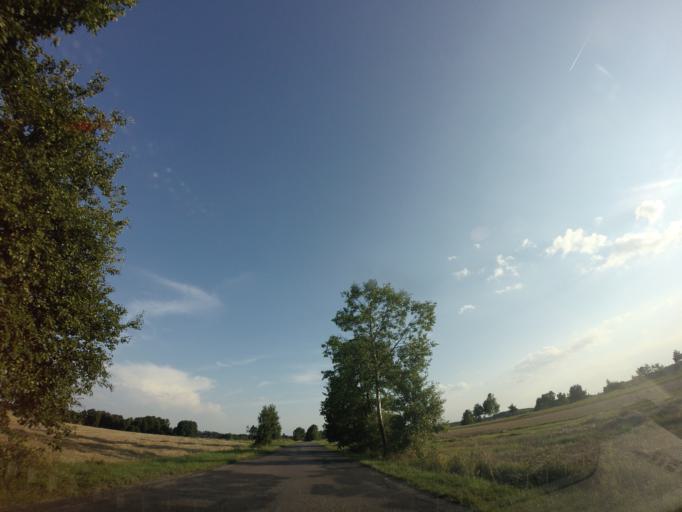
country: PL
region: Lublin Voivodeship
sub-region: Powiat pulawski
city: Kurow
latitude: 51.4217
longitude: 22.2028
